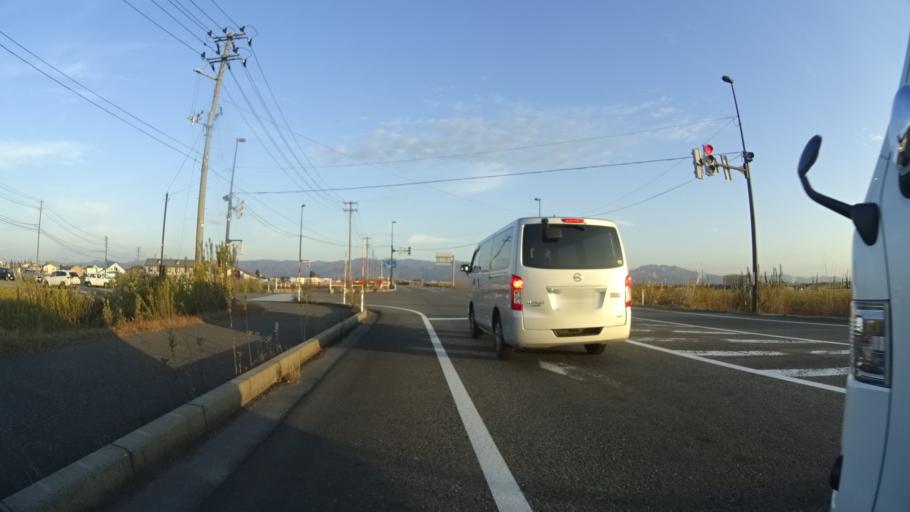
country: JP
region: Niigata
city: Nagaoka
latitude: 37.4355
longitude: 138.8058
